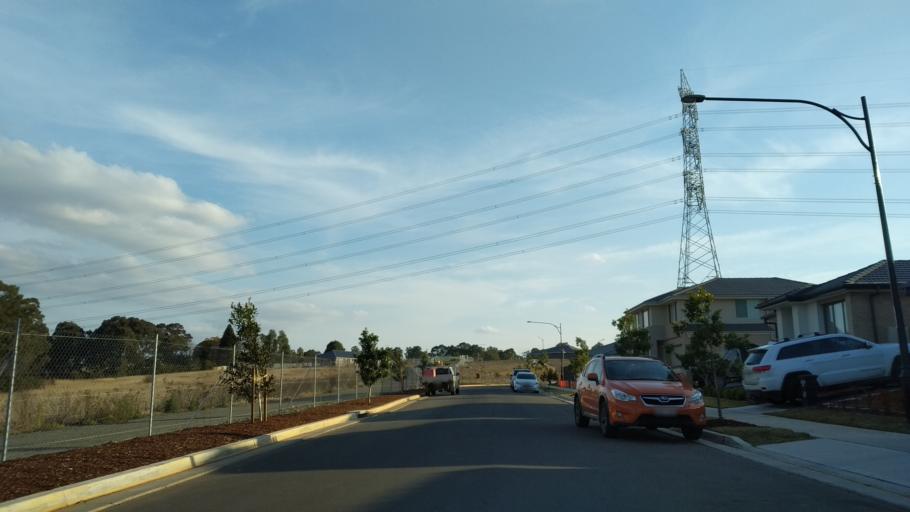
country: AU
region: New South Wales
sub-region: Penrith Municipality
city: Werrington County
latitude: -33.7388
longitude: 150.7524
